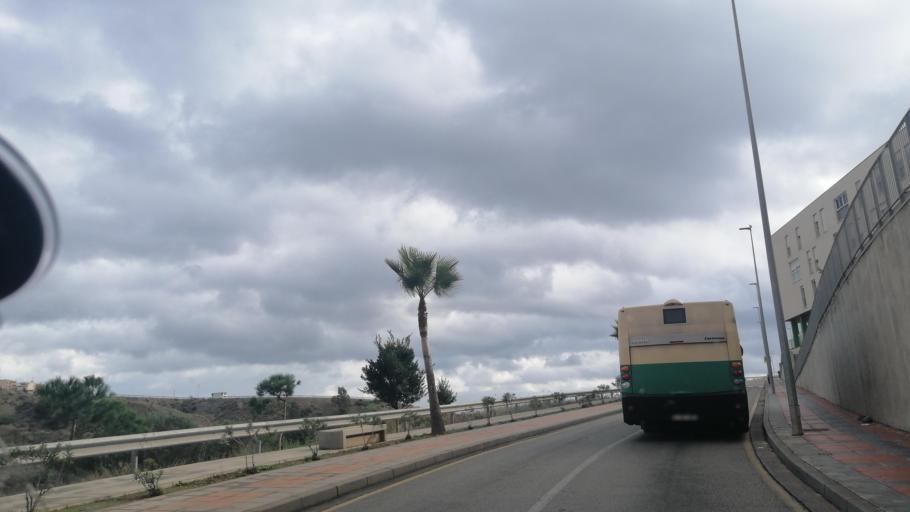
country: ES
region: Ceuta
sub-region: Ceuta
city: Ceuta
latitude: 35.8822
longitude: -5.3413
